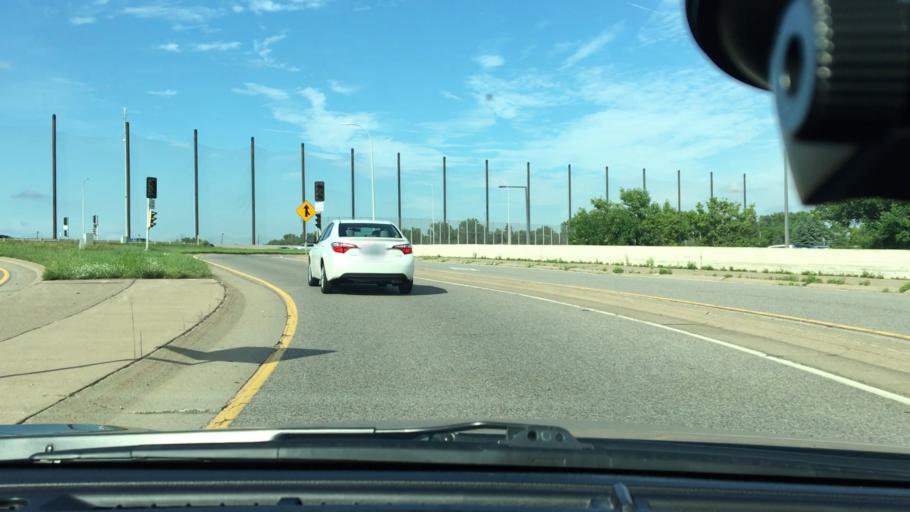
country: US
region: Minnesota
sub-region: Hennepin County
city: Saint Louis Park
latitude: 44.9728
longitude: -93.3899
